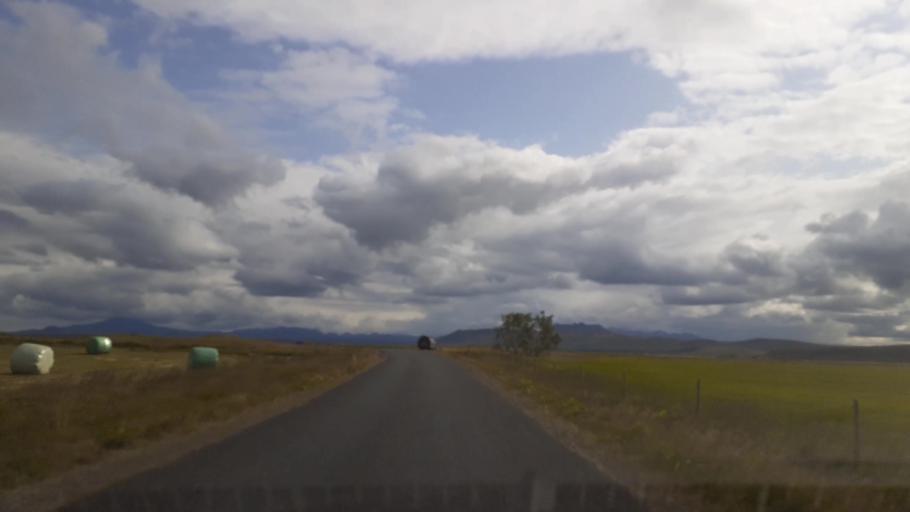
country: IS
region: South
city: Vestmannaeyjar
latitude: 63.7717
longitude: -20.2794
